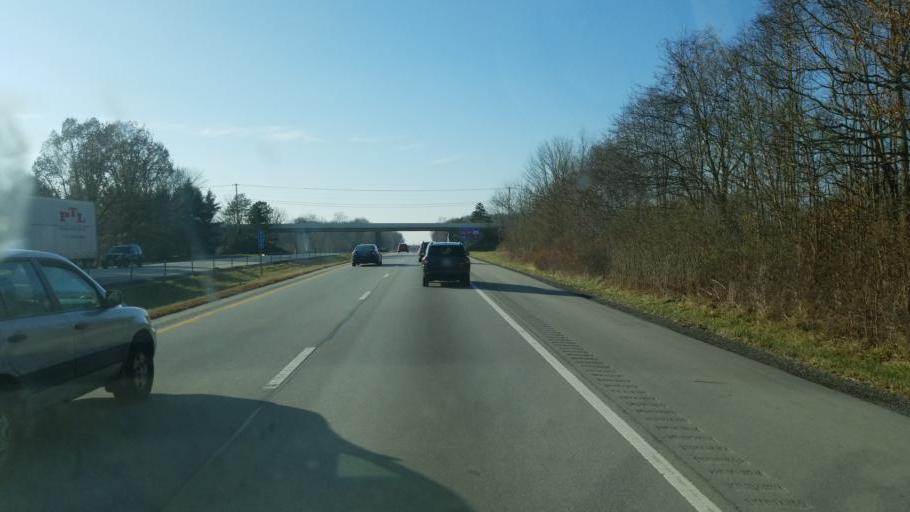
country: US
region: Ohio
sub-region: Medina County
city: Wadsworth
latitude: 41.0472
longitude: -81.7109
